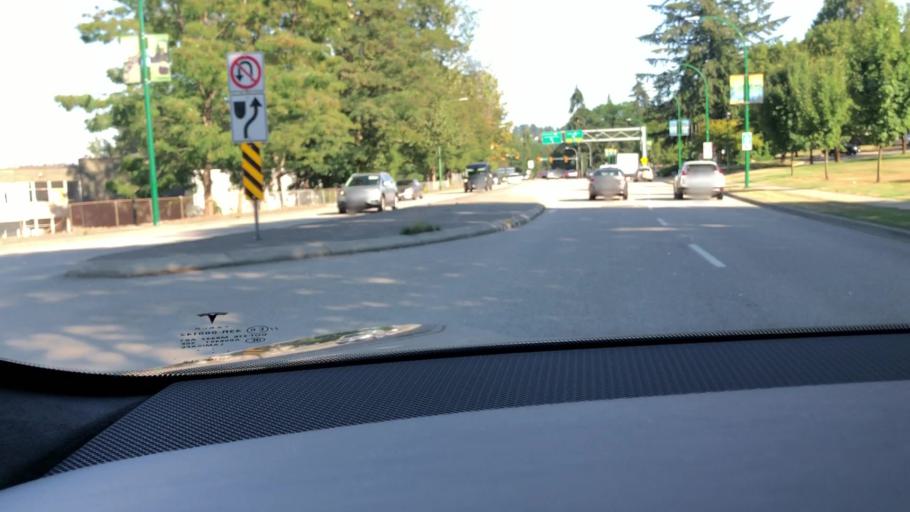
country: CA
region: British Columbia
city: Burnaby
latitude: 49.2432
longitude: -122.9708
